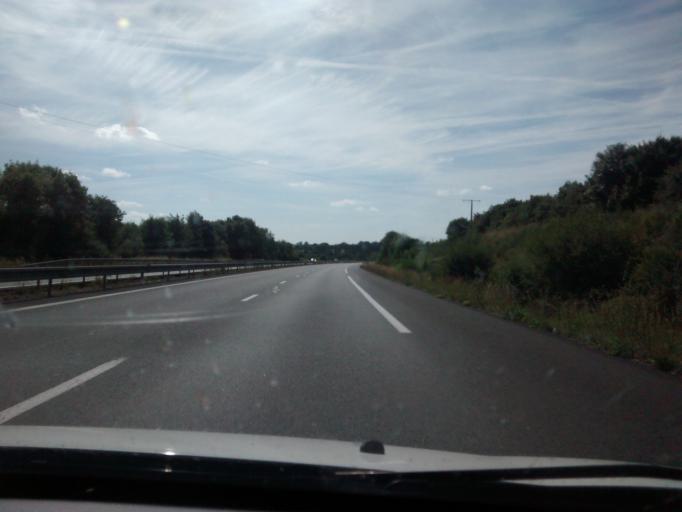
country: FR
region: Pays de la Loire
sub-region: Departement de la Mayenne
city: Argentre
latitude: 48.0746
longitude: -0.6346
